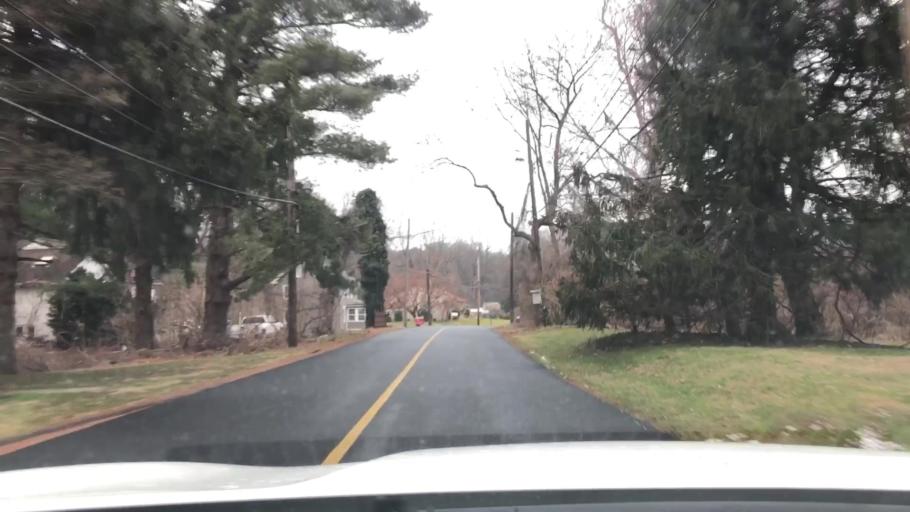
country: US
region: Pennsylvania
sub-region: Chester County
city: Spring City
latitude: 40.1976
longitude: -75.5798
